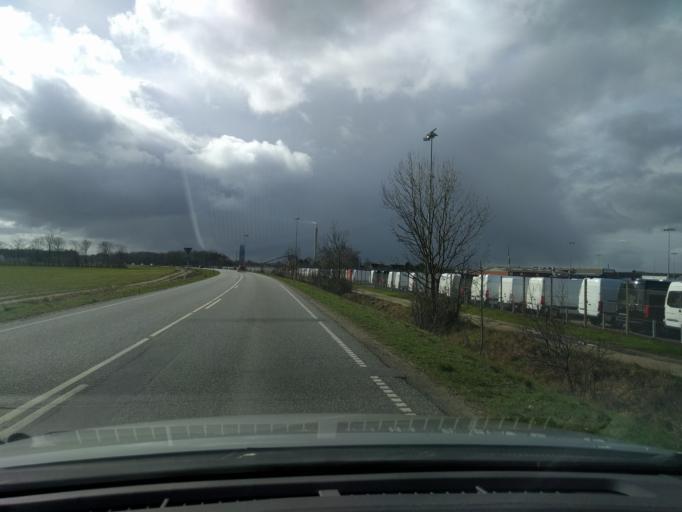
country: DK
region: South Denmark
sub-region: Kolding Kommune
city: Vamdrup
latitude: 55.4350
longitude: 9.3162
